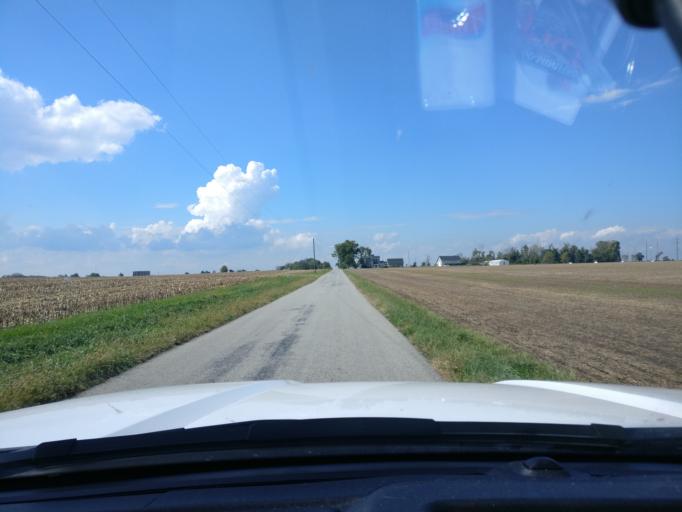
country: US
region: Ohio
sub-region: Warren County
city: Waynesville
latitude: 39.4637
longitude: -83.9725
